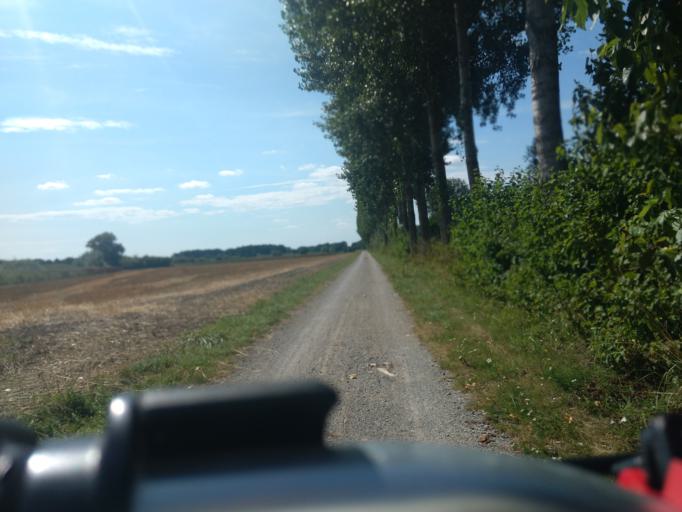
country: DE
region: North Rhine-Westphalia
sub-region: Regierungsbezirk Detmold
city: Hovelhof
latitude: 51.7661
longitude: 8.6307
